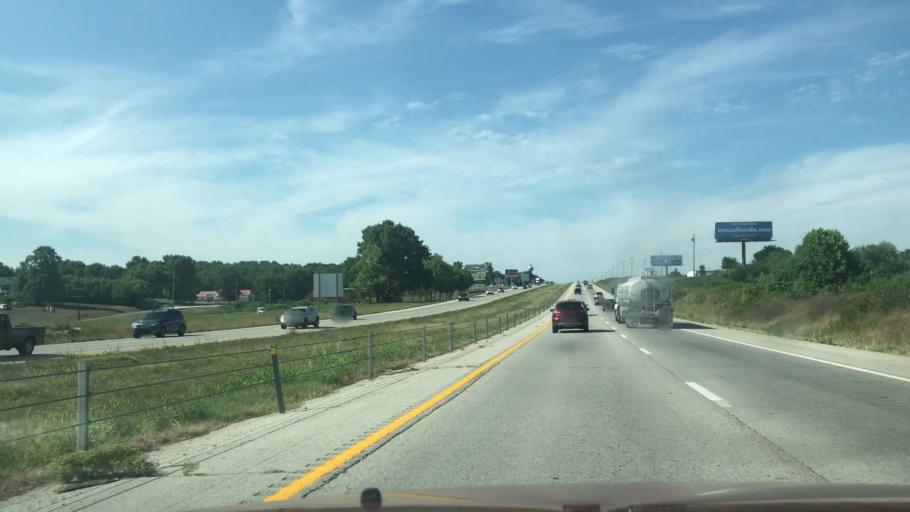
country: US
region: Missouri
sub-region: Christian County
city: Ozark
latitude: 37.0369
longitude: -93.2275
